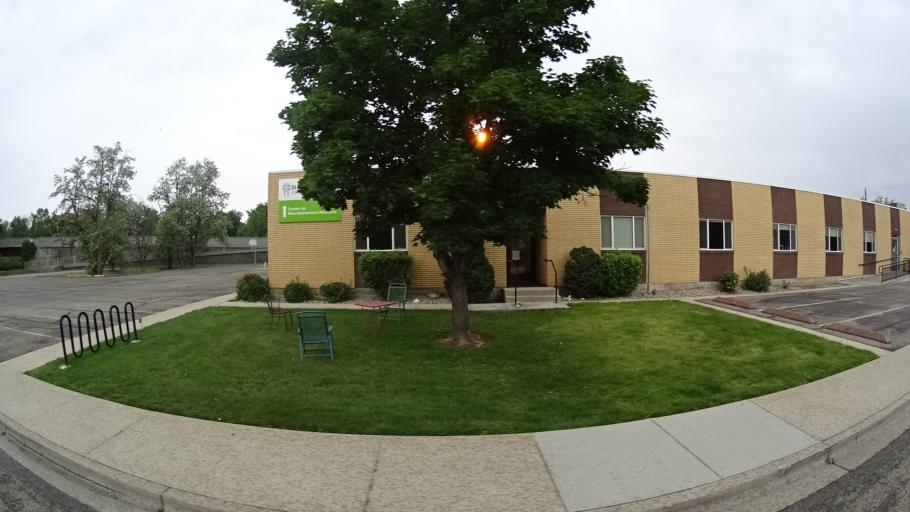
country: US
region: Idaho
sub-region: Ada County
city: Boise
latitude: 43.6016
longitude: -116.1875
